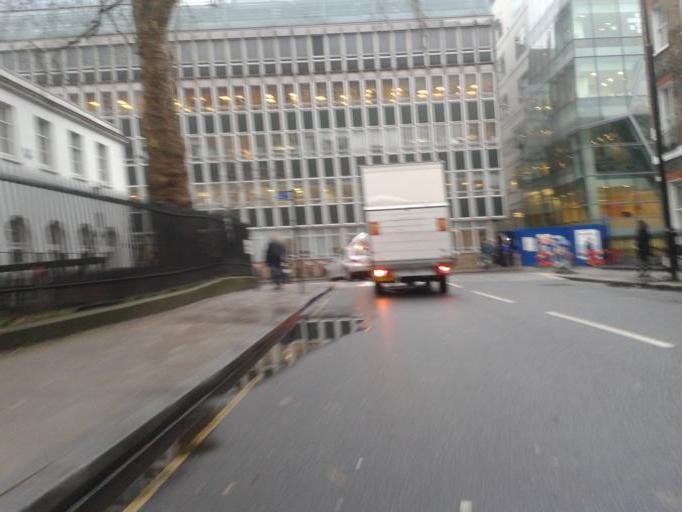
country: GB
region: England
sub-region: Greater London
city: Clerkenwell
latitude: 51.5237
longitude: -0.1207
